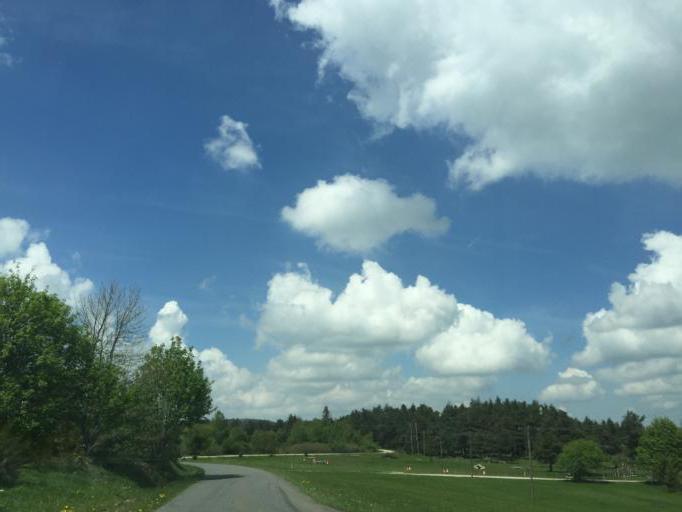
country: FR
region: Rhone-Alpes
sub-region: Departement de la Loire
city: Saint-Sauveur-en-Rue
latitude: 45.2925
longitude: 4.4820
